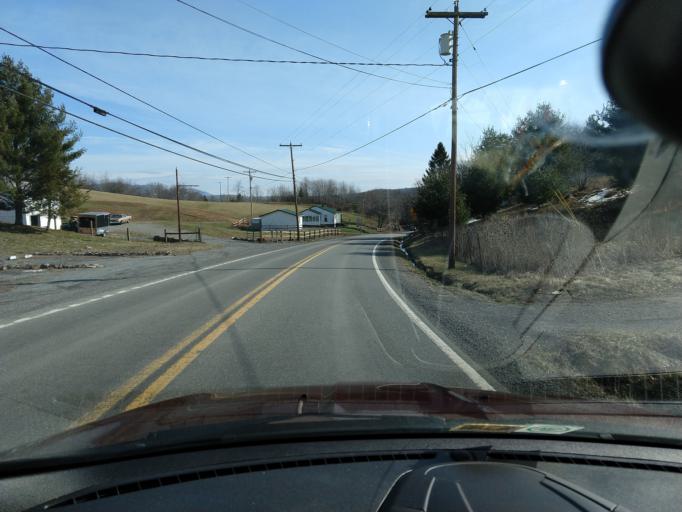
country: US
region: West Virginia
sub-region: Pocahontas County
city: Marlinton
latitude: 38.2086
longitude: -80.1064
